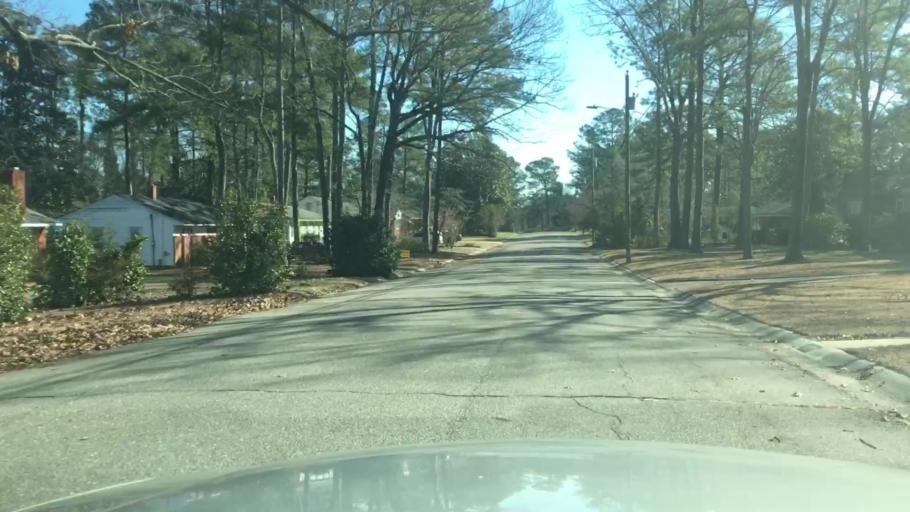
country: US
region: North Carolina
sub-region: Cumberland County
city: Fayetteville
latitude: 35.0785
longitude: -78.9189
